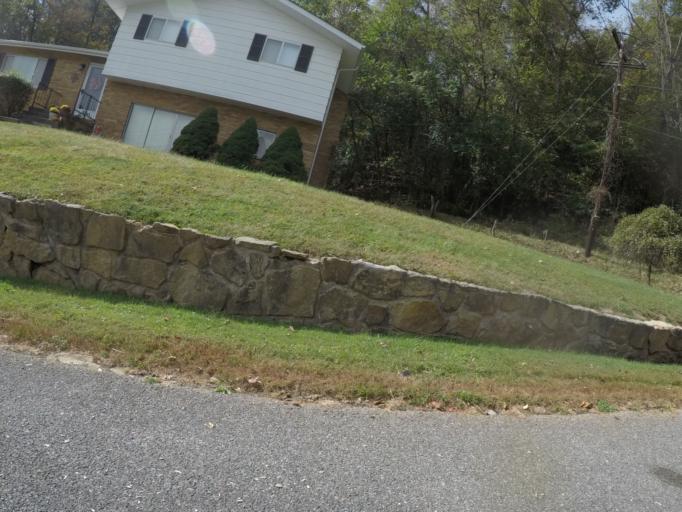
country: US
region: West Virginia
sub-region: Cabell County
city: Huntington
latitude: 38.3973
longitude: -82.3914
